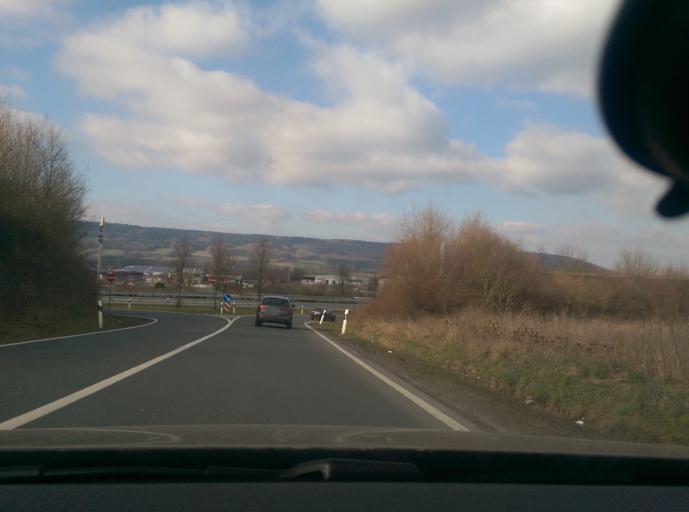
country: DE
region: Lower Saxony
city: Rehren
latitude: 52.2317
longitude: 9.2485
